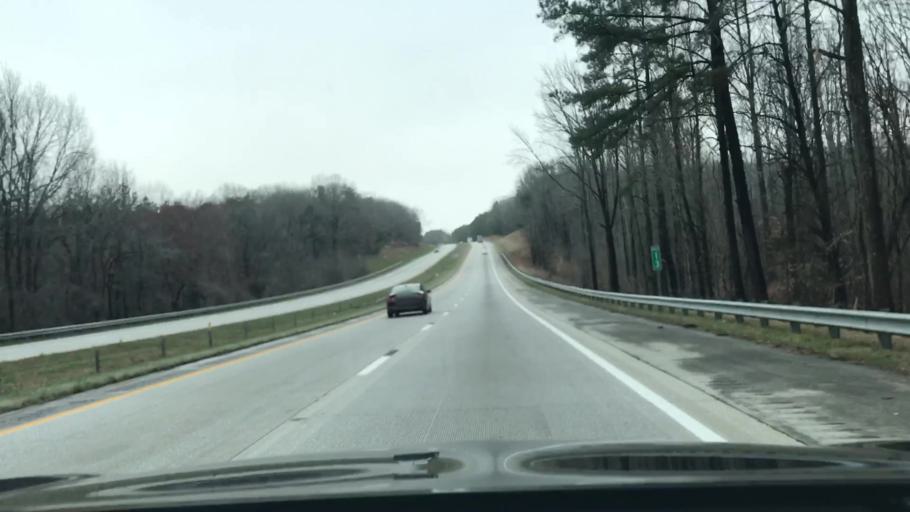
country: US
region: South Carolina
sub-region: Laurens County
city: Laurens
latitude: 34.5988
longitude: -82.0587
